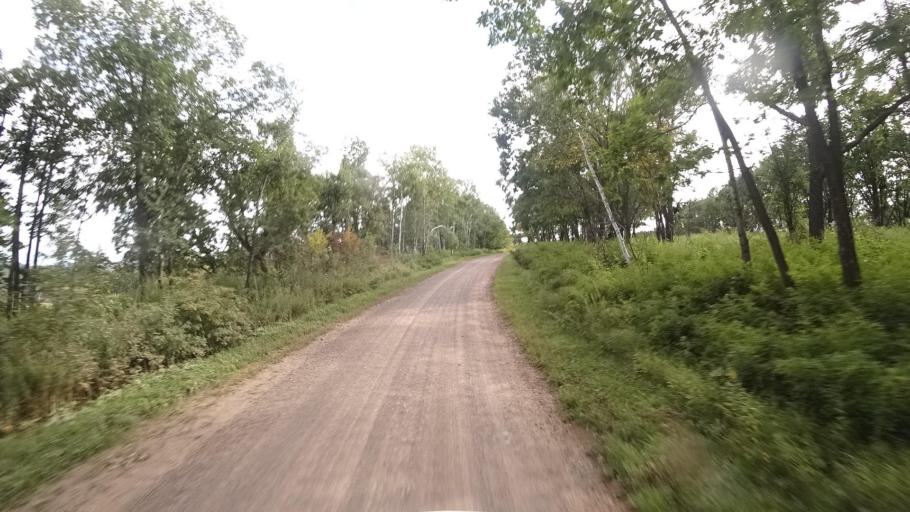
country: RU
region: Primorskiy
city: Dostoyevka
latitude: 44.3620
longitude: 133.5214
